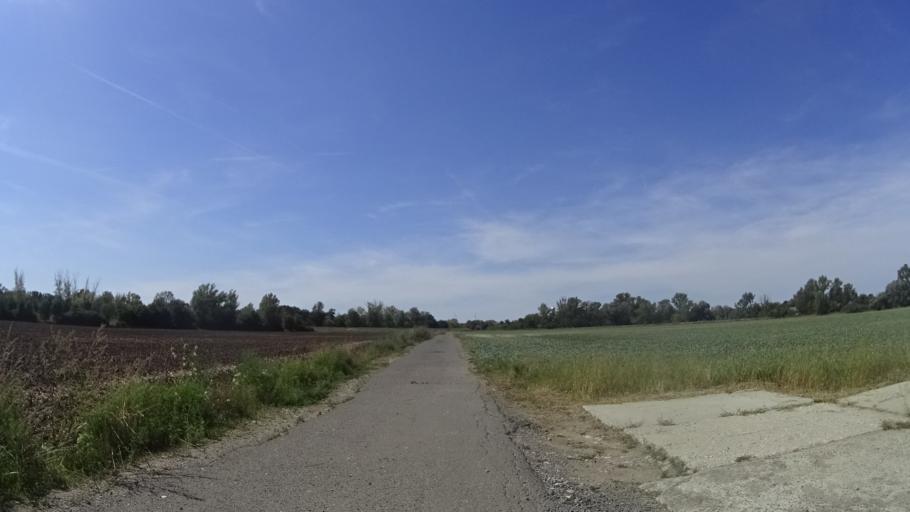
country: AT
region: Lower Austria
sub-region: Politischer Bezirk Ganserndorf
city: Angern an der March
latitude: 48.3737
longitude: 16.8493
